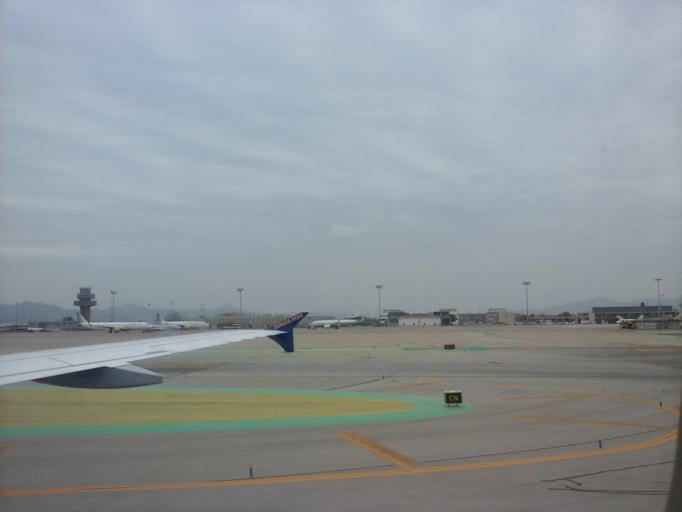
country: ES
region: Catalonia
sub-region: Provincia de Barcelona
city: El Prat de Llobregat
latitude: 41.3032
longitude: 2.0890
